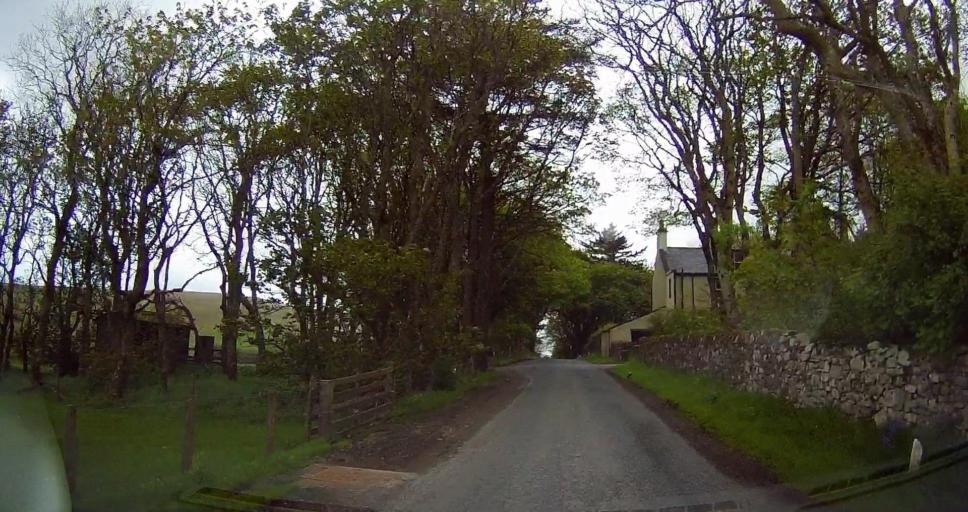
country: GB
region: Scotland
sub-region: Shetland Islands
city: Lerwick
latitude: 60.2708
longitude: -1.2870
